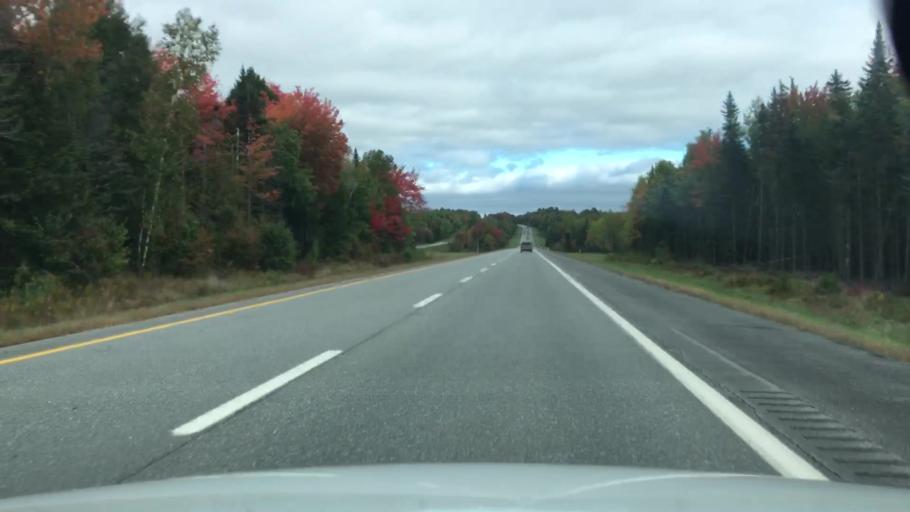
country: US
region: Maine
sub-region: Penobscot County
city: Carmel
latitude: 44.7764
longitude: -69.0501
